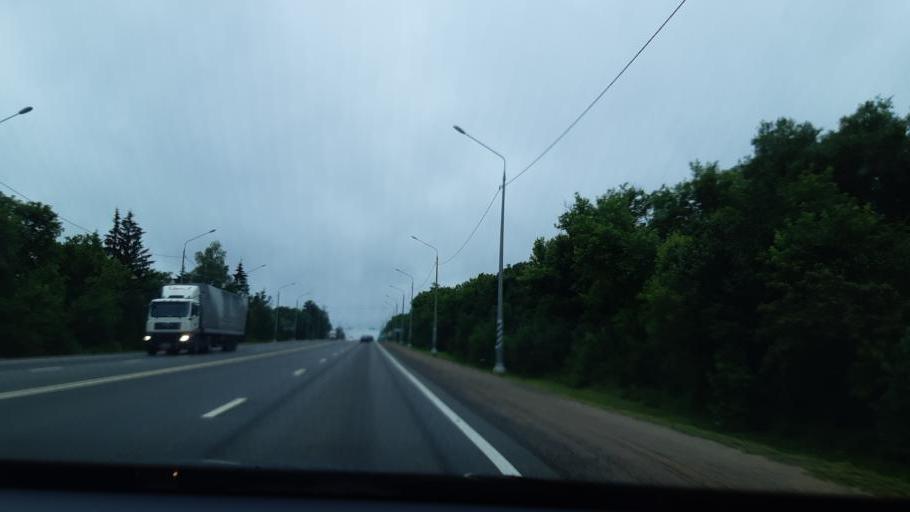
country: RU
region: Smolensk
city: Talashkino
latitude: 54.7133
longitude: 32.1107
